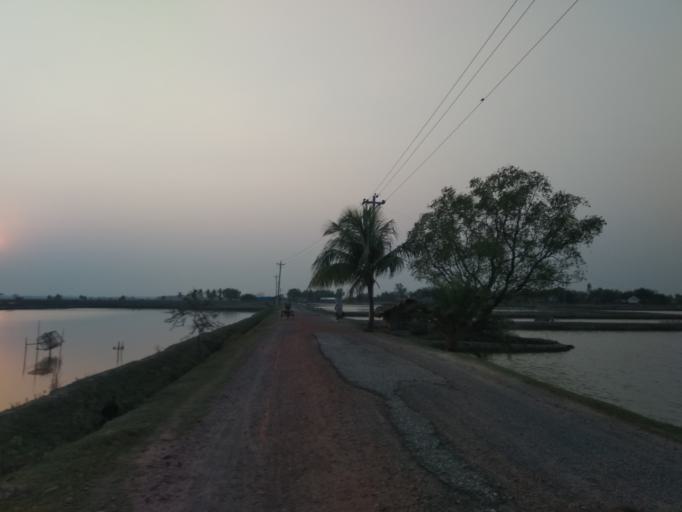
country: IN
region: West Bengal
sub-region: North 24 Parganas
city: Taki
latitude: 22.4555
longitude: 89.0768
